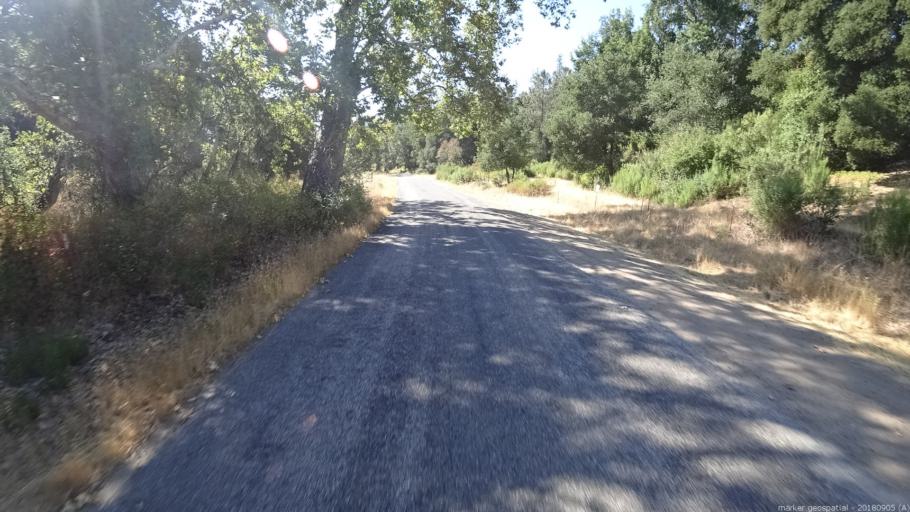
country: US
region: California
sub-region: Monterey County
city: Gonzales
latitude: 36.3437
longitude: -121.5402
